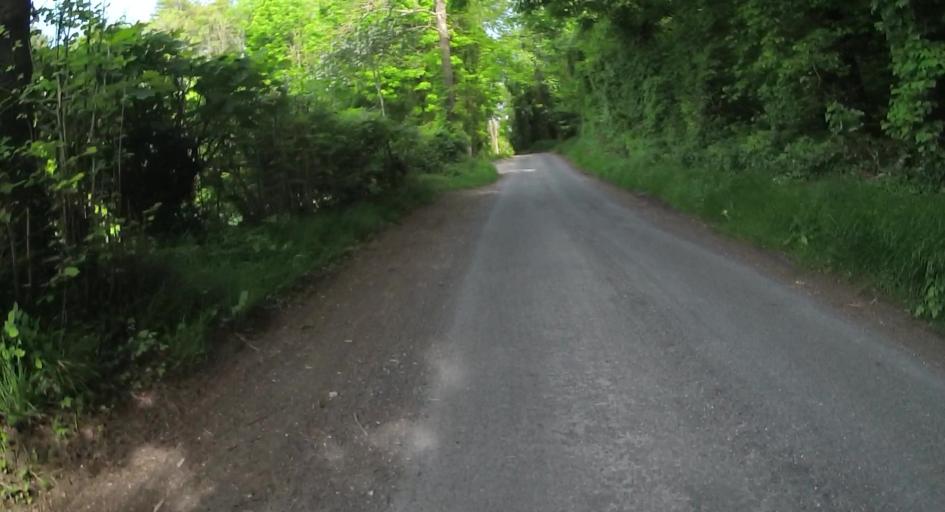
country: GB
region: England
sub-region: West Berkshire
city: Greenham
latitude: 51.3317
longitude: -1.3072
